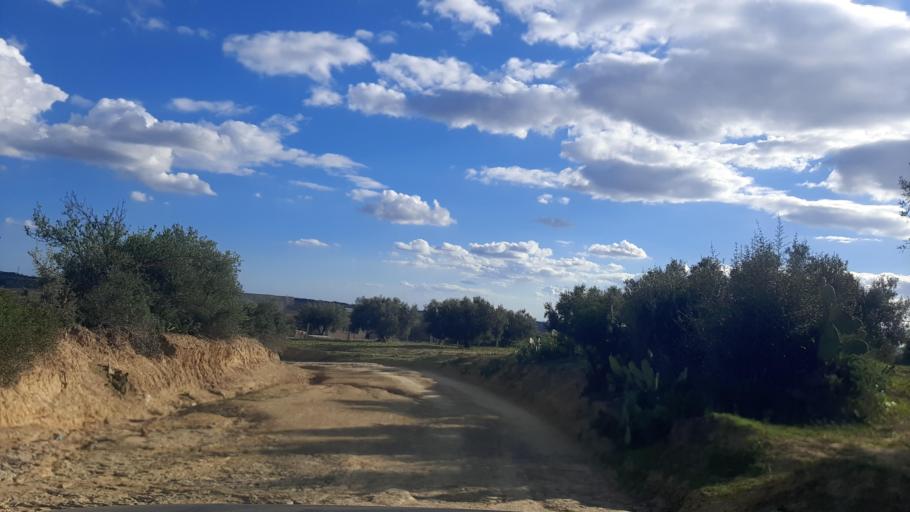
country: TN
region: Nabul
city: Bu `Urqub
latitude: 36.4577
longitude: 10.4935
